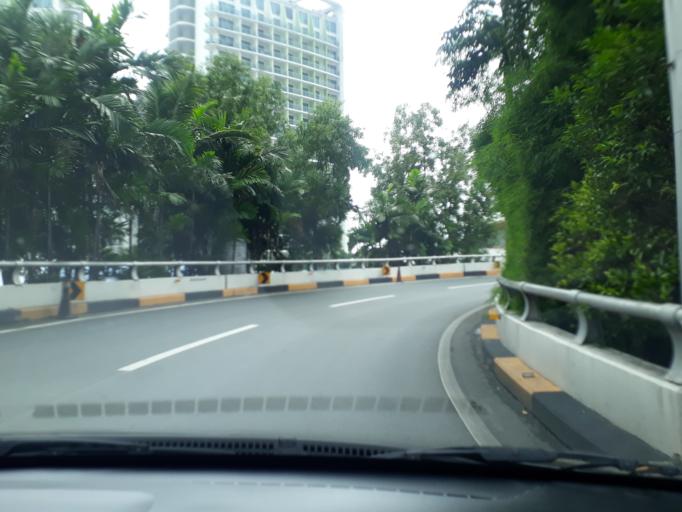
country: PH
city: Sambayanihan People's Village
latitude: 14.4856
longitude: 121.0422
